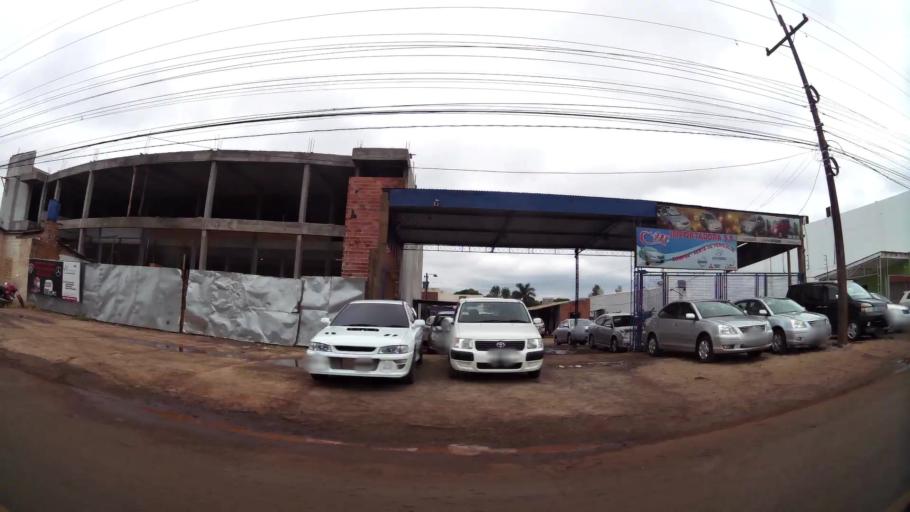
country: PY
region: Alto Parana
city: Ciudad del Este
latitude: -25.4963
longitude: -54.6846
